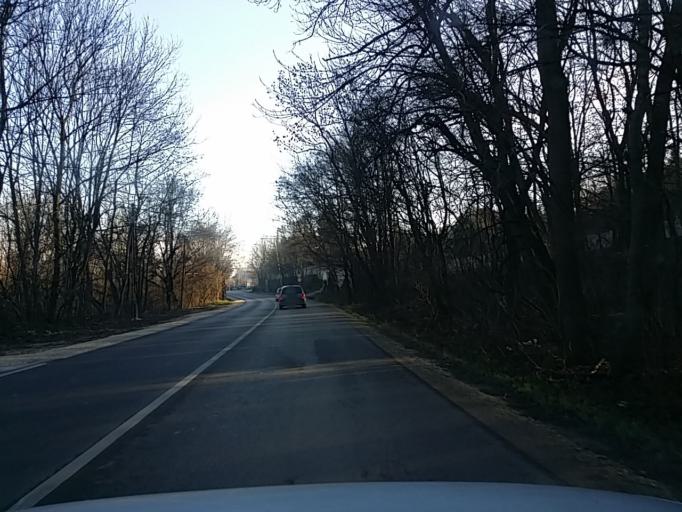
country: HU
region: Pest
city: Solymar
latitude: 47.5603
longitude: 18.9186
